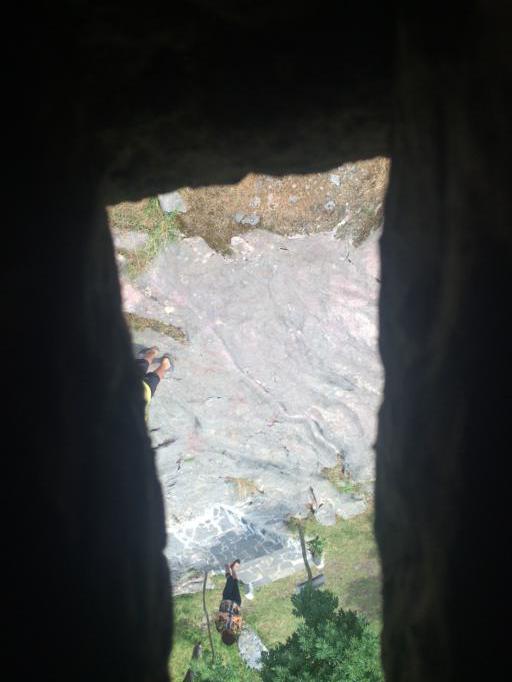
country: AL
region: Shkoder
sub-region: Rrethi i Shkodres
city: Nicaj-Shale
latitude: 42.3857
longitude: 19.7826
